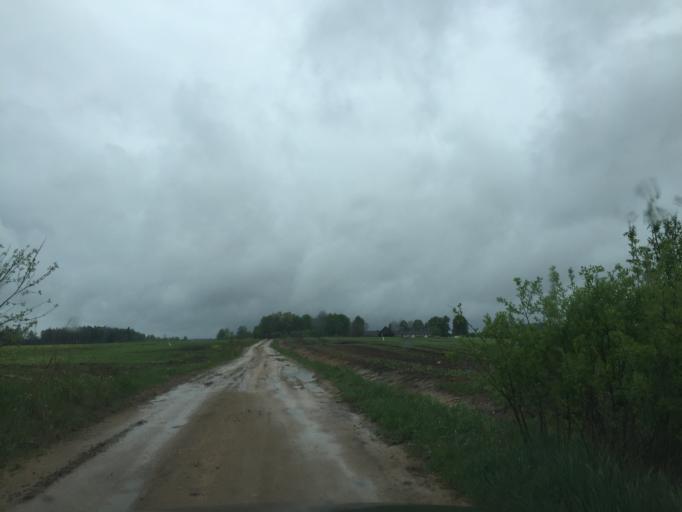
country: LV
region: Ogre
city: Jumprava
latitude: 56.6604
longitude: 25.0111
